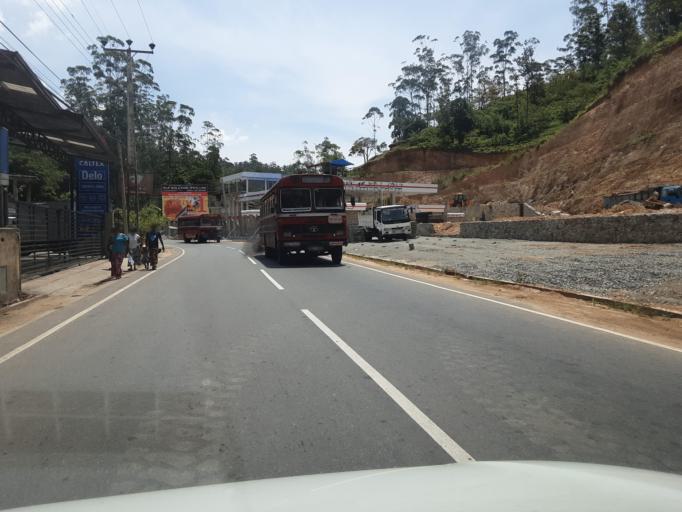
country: LK
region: Central
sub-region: Nuwara Eliya District
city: Nuwara Eliya
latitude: 6.9105
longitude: 80.9060
